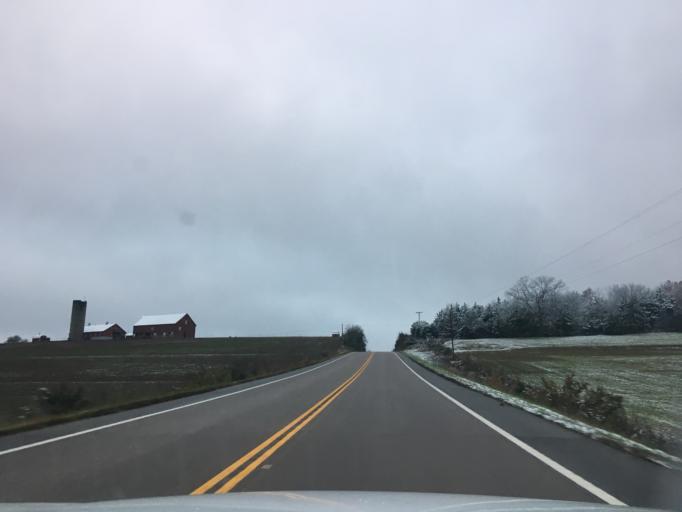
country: US
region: Missouri
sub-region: Osage County
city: Linn
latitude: 38.4686
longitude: -91.7682
